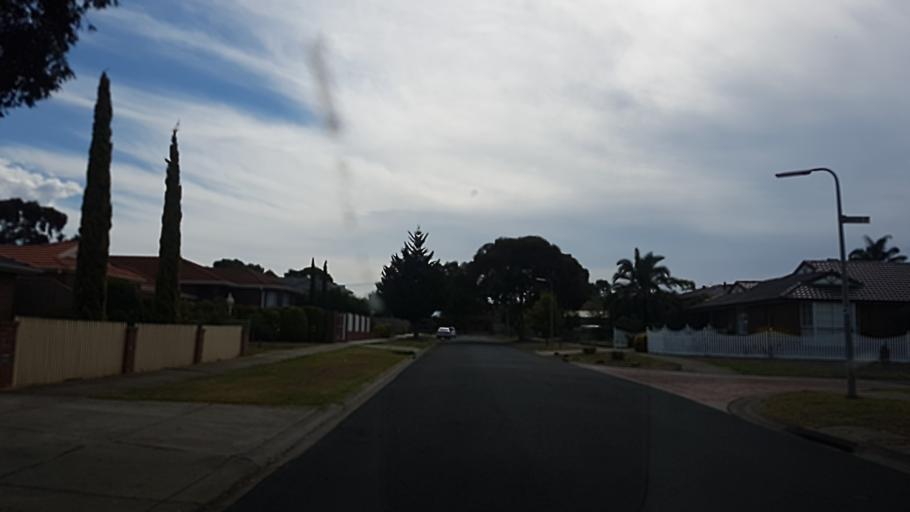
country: AU
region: Victoria
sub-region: Brimbank
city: Keilor Lodge
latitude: -37.7002
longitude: 144.7982
